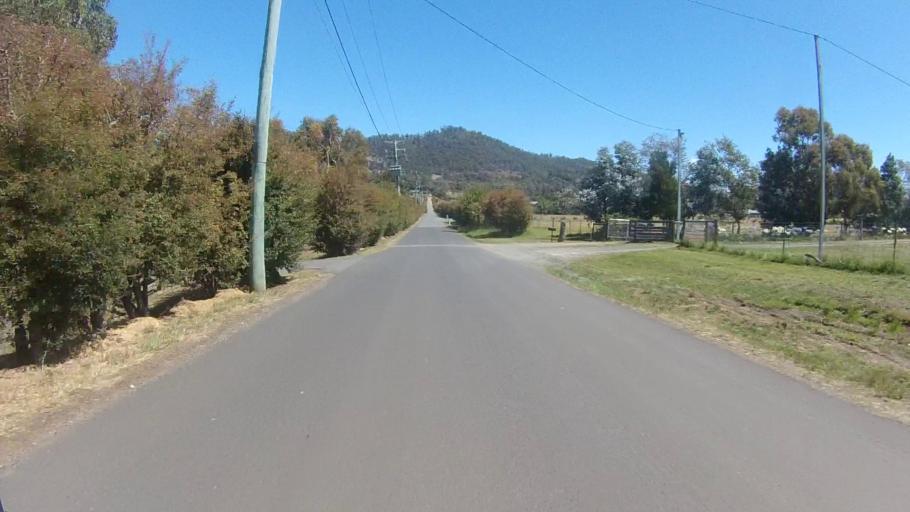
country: AU
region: Tasmania
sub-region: Clarence
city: Cambridge
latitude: -42.8418
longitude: 147.4613
